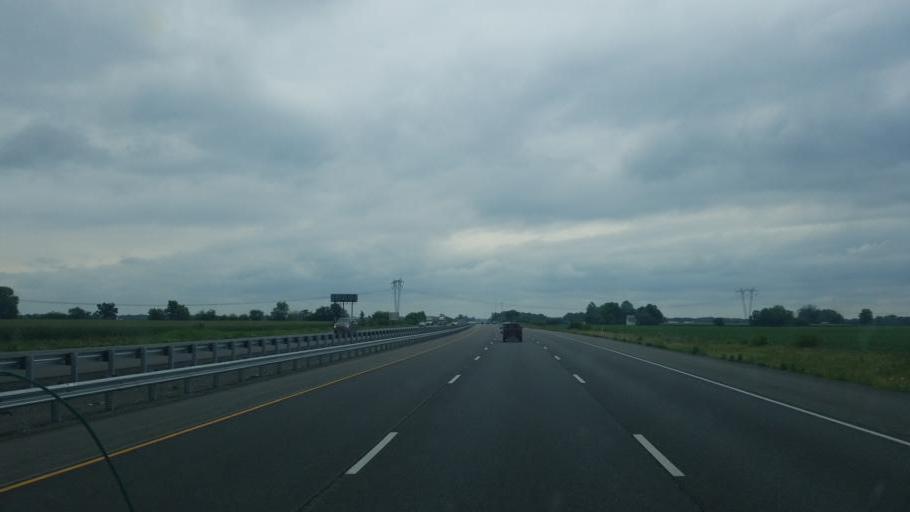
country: US
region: Indiana
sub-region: Madison County
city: Ingalls
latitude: 39.9911
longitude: -85.8234
